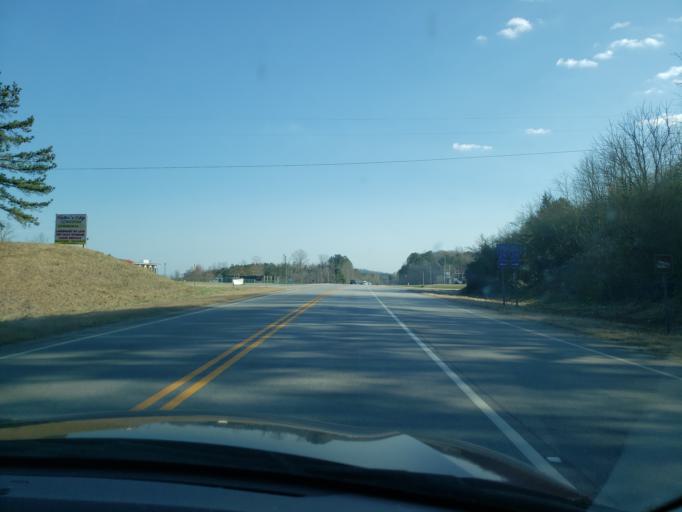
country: US
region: Alabama
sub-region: Randolph County
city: Wedowee
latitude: 33.4259
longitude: -85.5519
